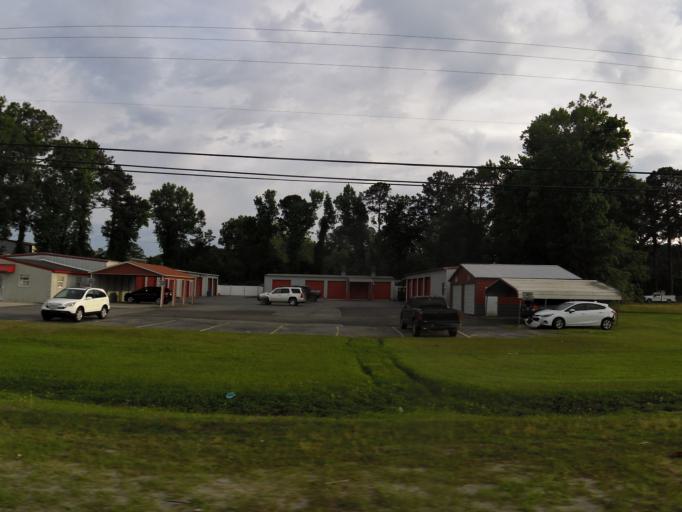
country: US
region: Georgia
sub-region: Chatham County
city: Pooler
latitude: 32.0939
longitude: -81.2027
